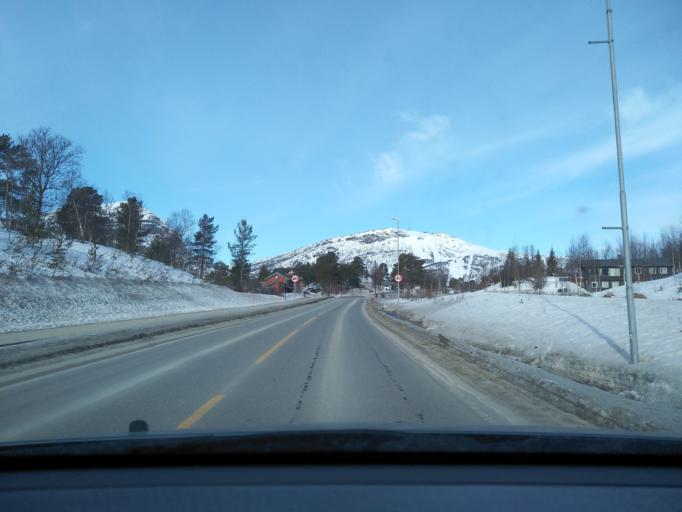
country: NO
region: Aust-Agder
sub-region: Bykle
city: Hovden
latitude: 59.5569
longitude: 7.3597
